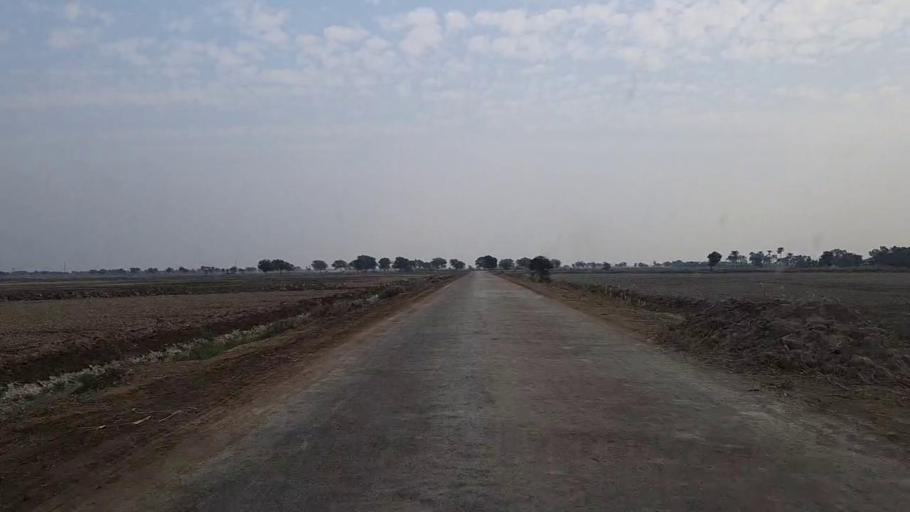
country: PK
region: Sindh
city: Mirwah Gorchani
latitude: 25.3928
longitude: 69.0789
